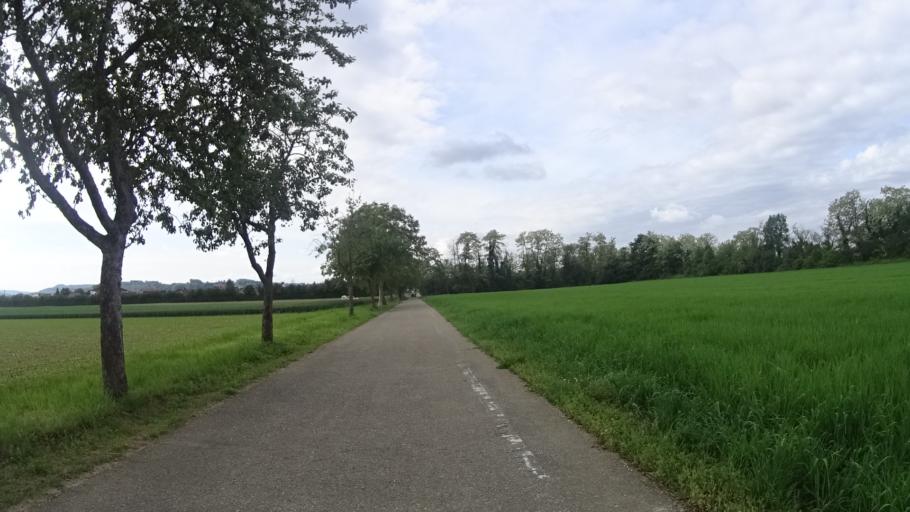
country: DE
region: Baden-Wuerttemberg
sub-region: Freiburg Region
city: Schliengen
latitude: 47.7755
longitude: 7.5529
